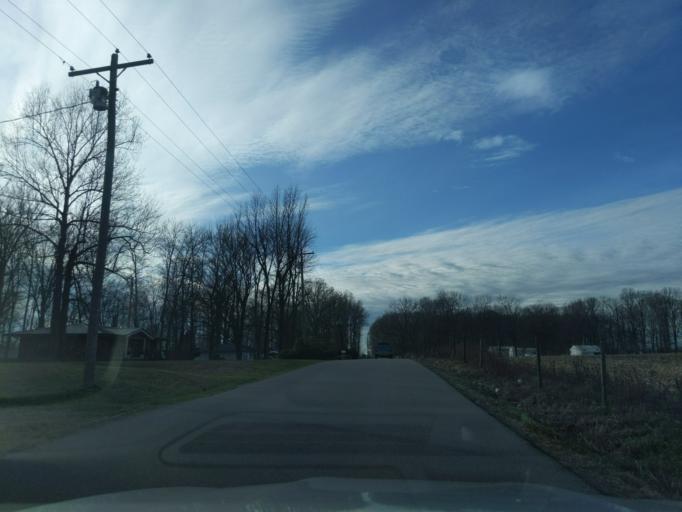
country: US
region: Indiana
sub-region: Decatur County
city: Westport
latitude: 39.1908
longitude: -85.5416
